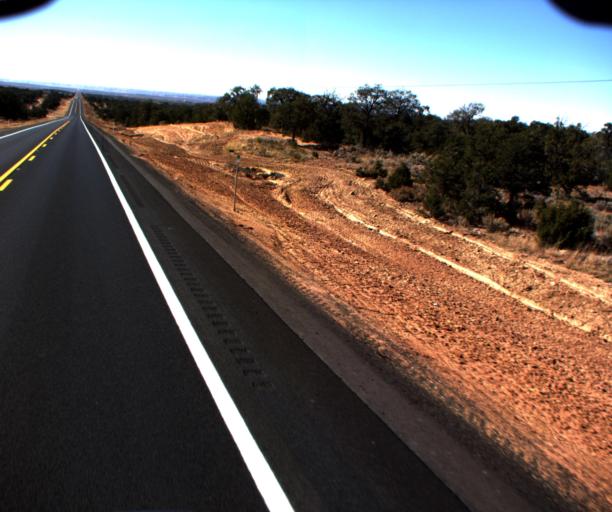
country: US
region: Arizona
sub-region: Apache County
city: Ganado
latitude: 35.7191
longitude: -109.3789
